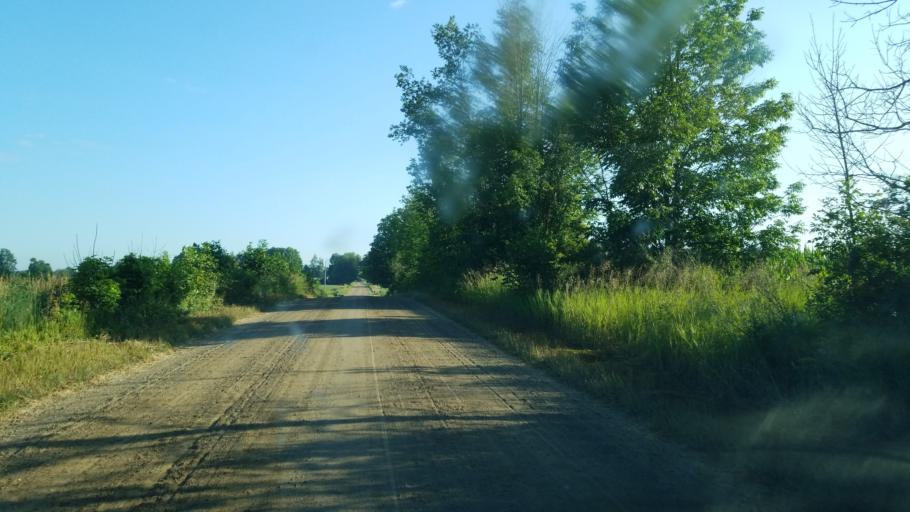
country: US
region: Michigan
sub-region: Mecosta County
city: Canadian Lakes
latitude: 43.5481
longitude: -85.3632
